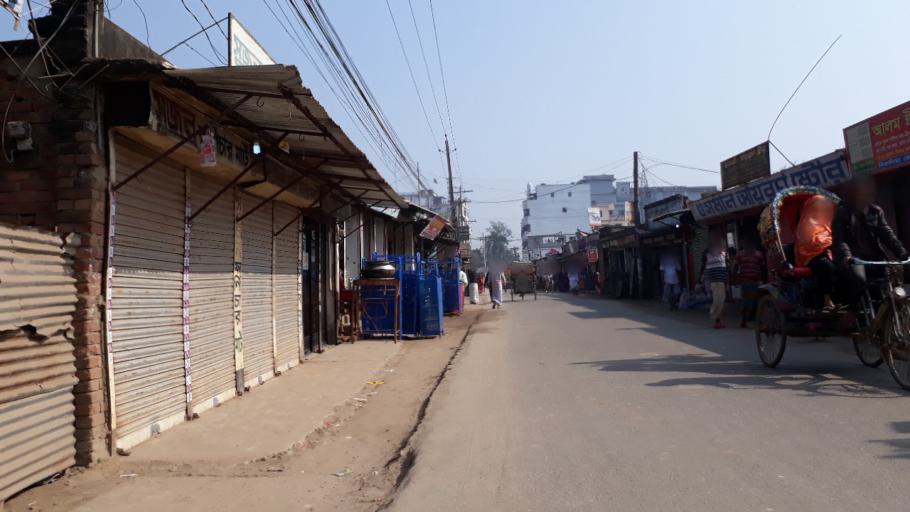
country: BD
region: Dhaka
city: Tungi
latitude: 23.8482
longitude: 90.2631
